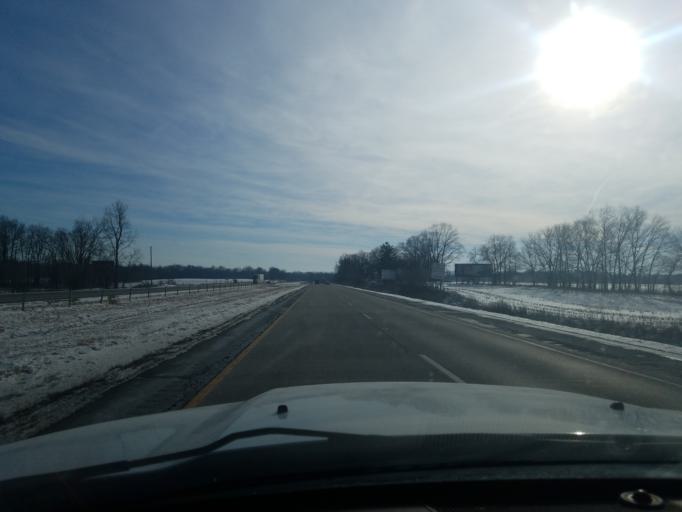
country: US
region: Indiana
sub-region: Grant County
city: Upland
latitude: 40.4680
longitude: -85.5503
